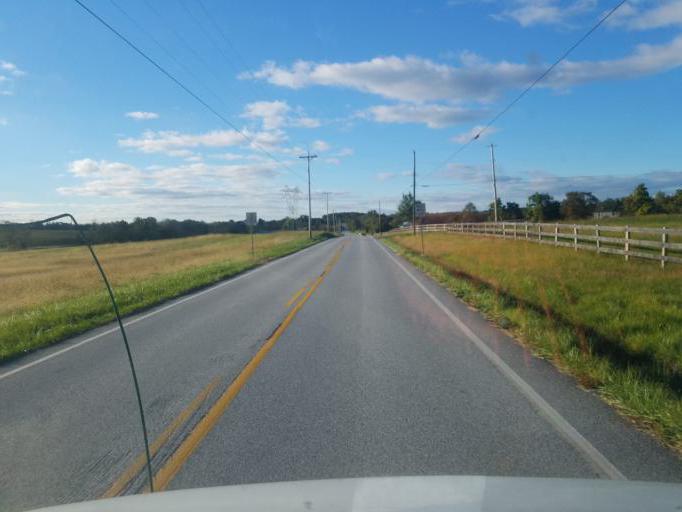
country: US
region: Pennsylvania
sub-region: Adams County
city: Gettysburg
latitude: 39.8822
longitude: -77.2295
